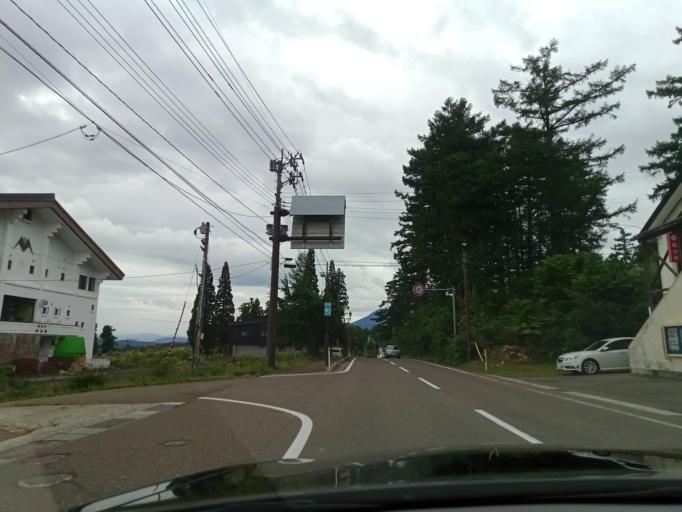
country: JP
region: Niigata
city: Arai
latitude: 36.8908
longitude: 138.1771
